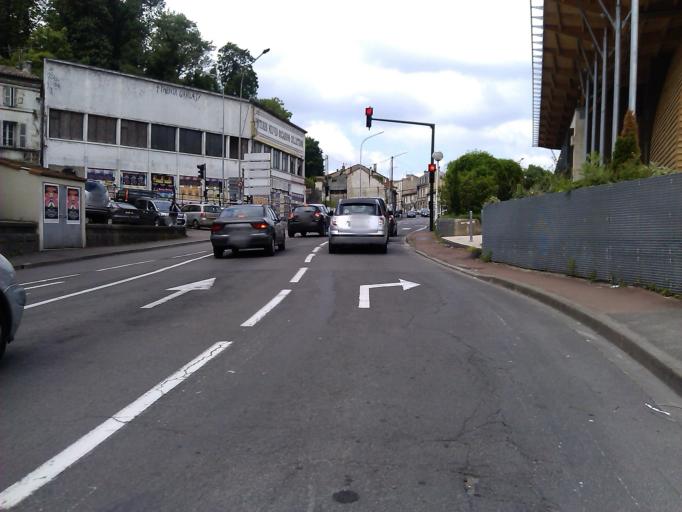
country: FR
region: Poitou-Charentes
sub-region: Departement de la Charente
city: Angouleme
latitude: 45.6535
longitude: 0.1491
